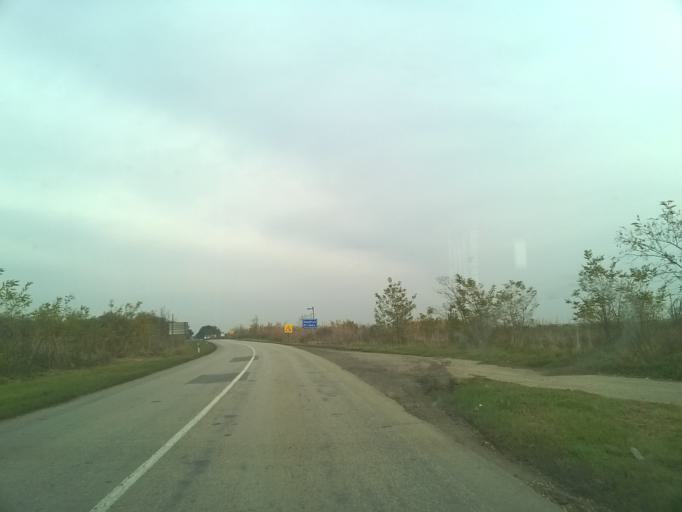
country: RS
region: Autonomna Pokrajina Vojvodina
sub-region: Juznobanatski Okrug
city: Pancevo
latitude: 44.9363
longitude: 20.6693
